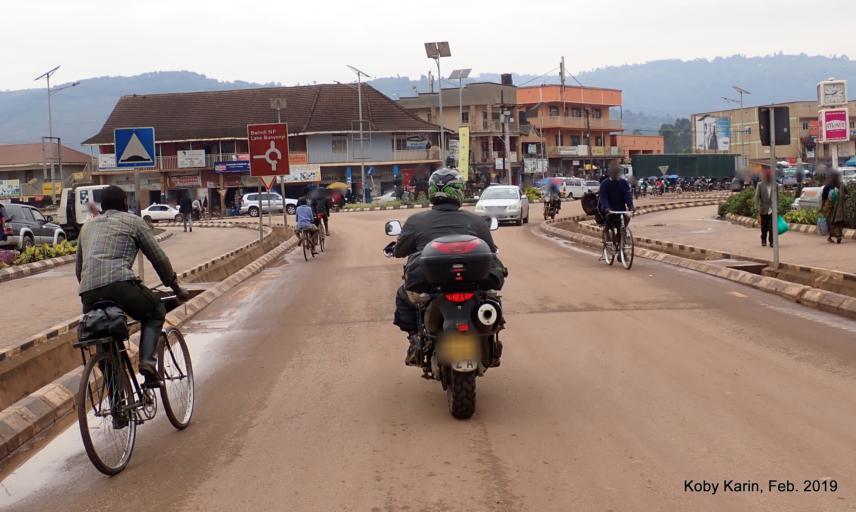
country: UG
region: Western Region
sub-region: Kabale District
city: Kabale
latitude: -1.2592
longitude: 29.9940
